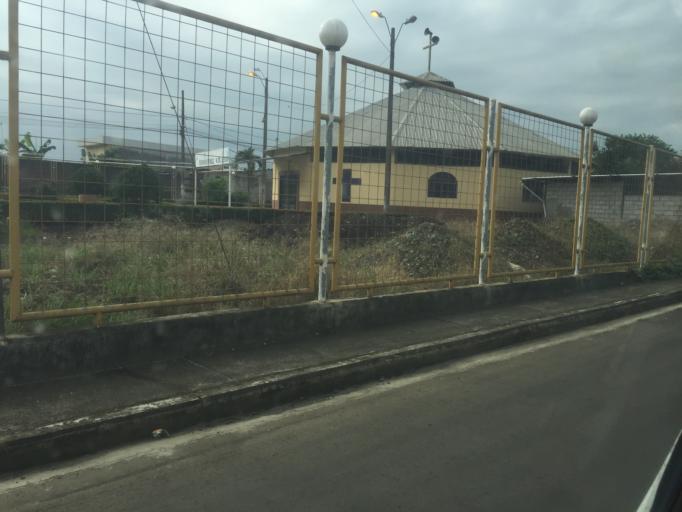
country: EC
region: Los Rios
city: Quevedo
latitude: -1.0533
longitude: -79.4814
